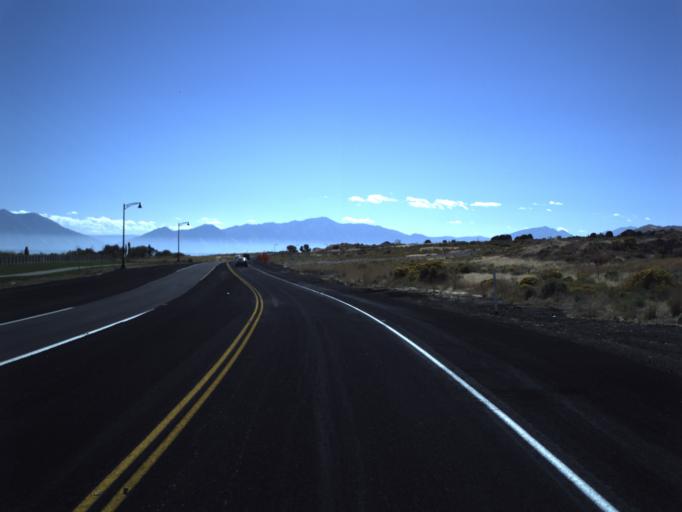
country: US
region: Utah
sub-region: Utah County
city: Saratoga Springs
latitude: 40.3099
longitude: -111.8909
